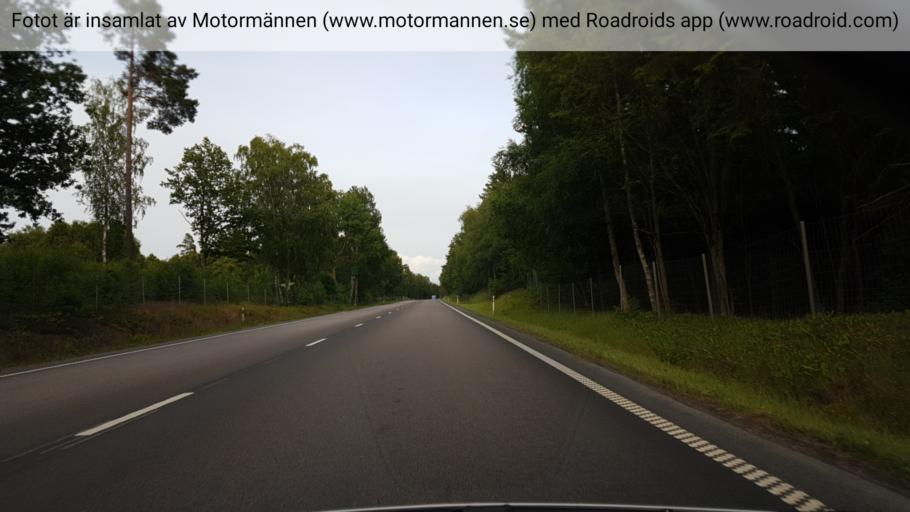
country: SE
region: Vaestra Goetaland
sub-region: Lidkopings Kommun
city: Vinninga
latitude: 58.4290
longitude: 13.3140
